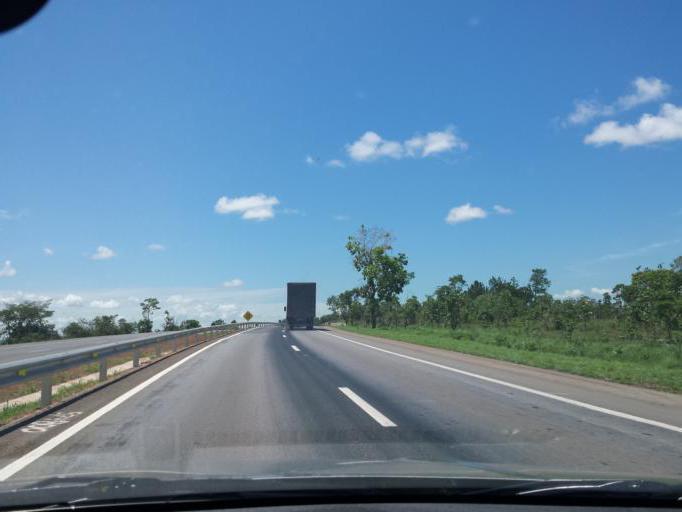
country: BR
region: Goias
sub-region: Luziania
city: Luziania
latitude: -16.5101
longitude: -47.8090
